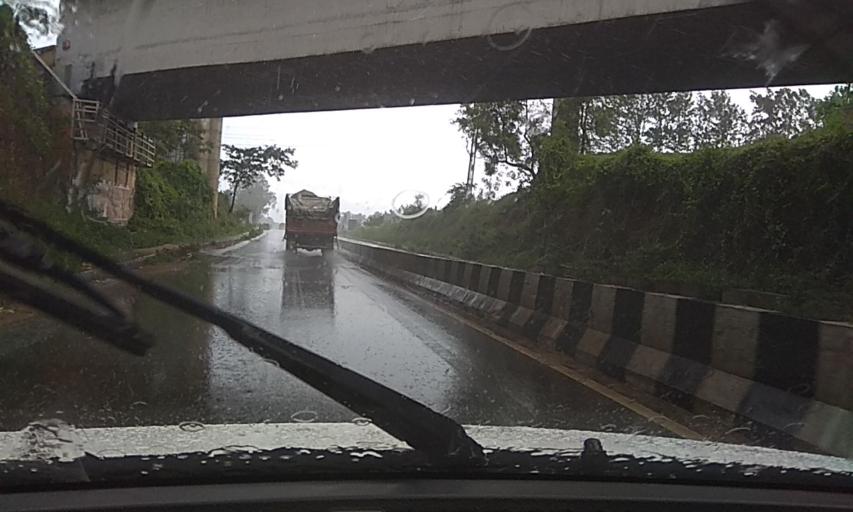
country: IN
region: Karnataka
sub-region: Mysore
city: Nanjangud
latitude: 12.1896
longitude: 76.6664
